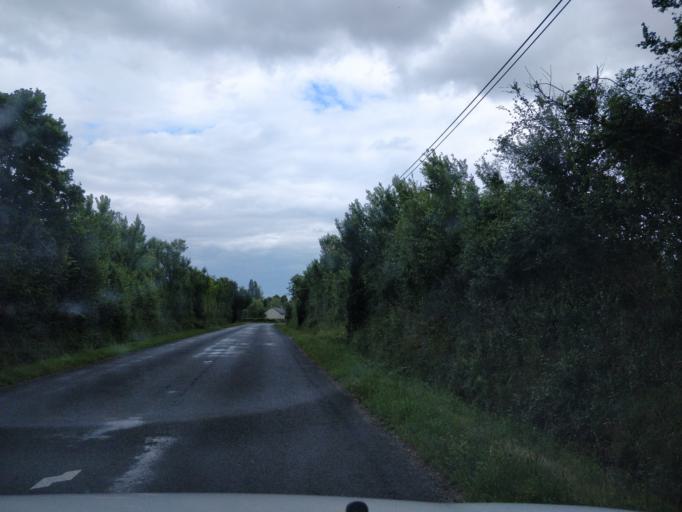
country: FR
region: Pays de la Loire
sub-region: Departement de Maine-et-Loire
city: Grez-Neuville
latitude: 47.6393
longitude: -0.6531
